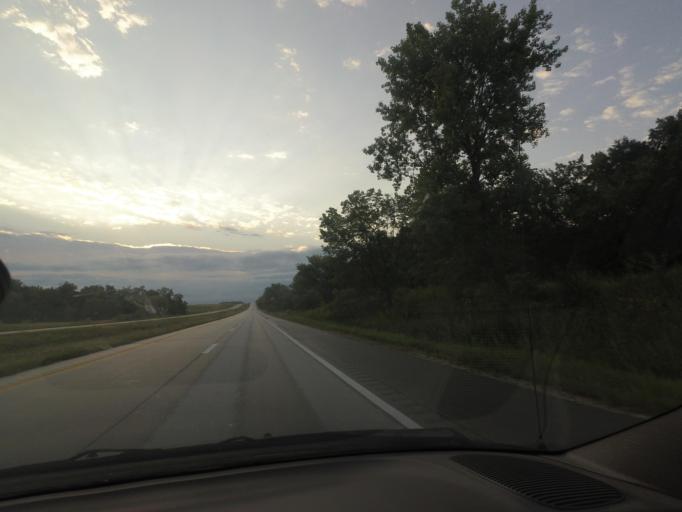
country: US
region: Missouri
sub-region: Shelby County
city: Shelbina
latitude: 39.7240
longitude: -92.1696
